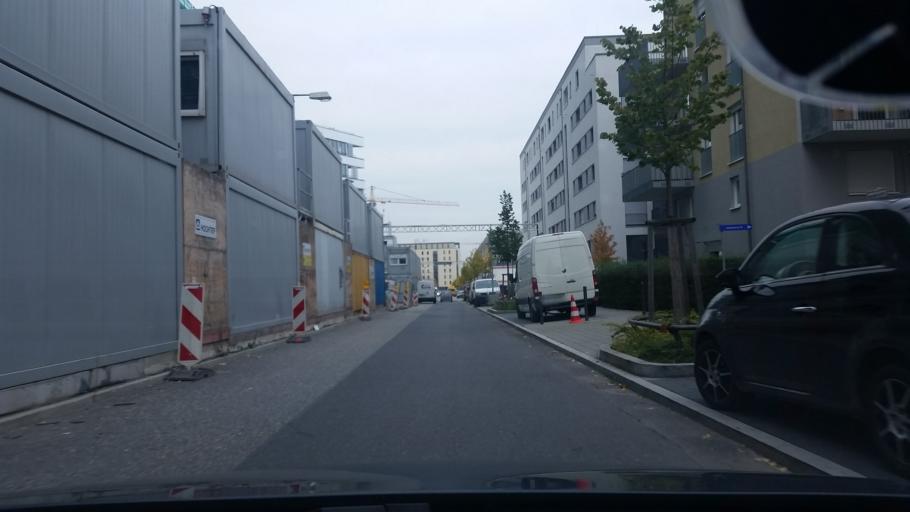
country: DE
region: Hesse
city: Niederrad
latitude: 50.1075
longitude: 8.6355
